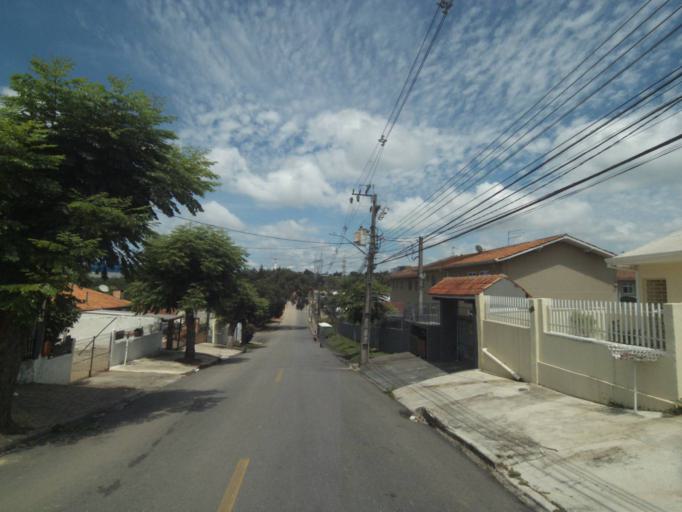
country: BR
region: Parana
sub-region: Curitiba
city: Curitiba
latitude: -25.4526
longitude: -49.3562
